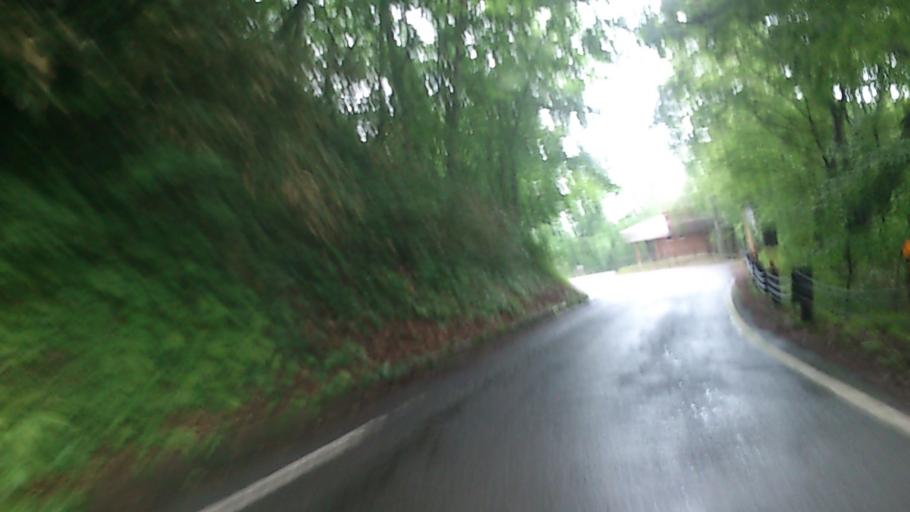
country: JP
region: Akita
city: Noshiromachi
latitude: 40.5631
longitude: 139.9686
